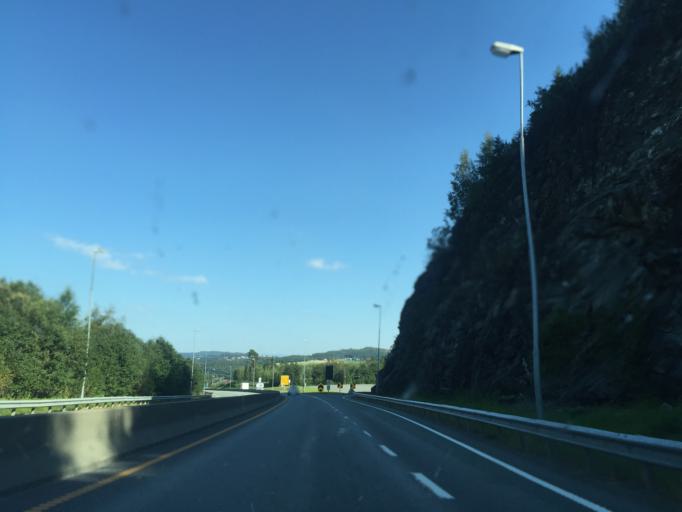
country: NO
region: Sor-Trondelag
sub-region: Malvik
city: Malvik
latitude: 63.4265
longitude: 10.6603
